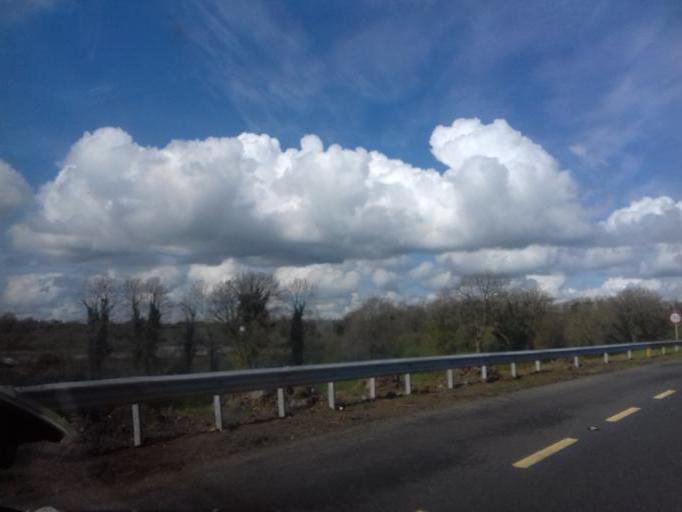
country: IE
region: Ulster
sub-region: An Cabhan
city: Belturbet
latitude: 54.0797
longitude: -7.4305
